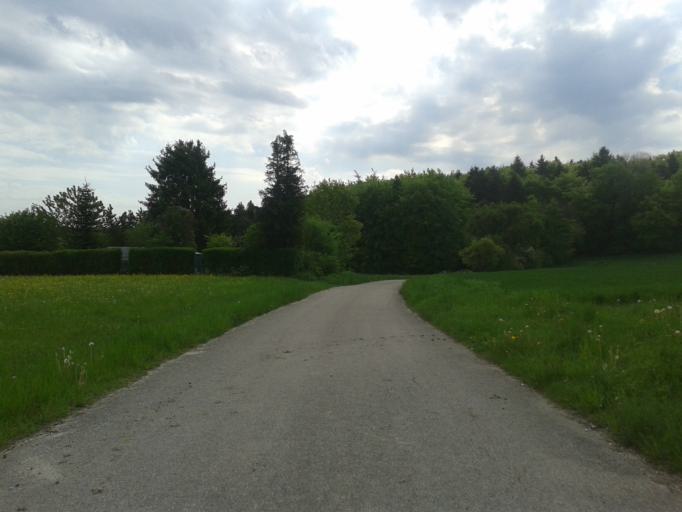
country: DE
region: Baden-Wuerttemberg
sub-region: Tuebingen Region
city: Blaubeuren
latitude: 48.3795
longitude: 9.8163
